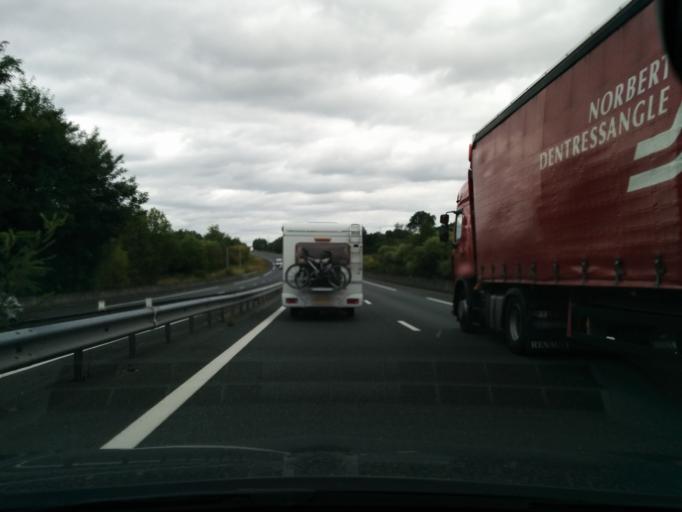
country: FR
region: Limousin
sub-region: Departement de la Haute-Vienne
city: Saint-Sulpice-les-Feuilles
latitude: 46.3791
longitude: 1.4471
